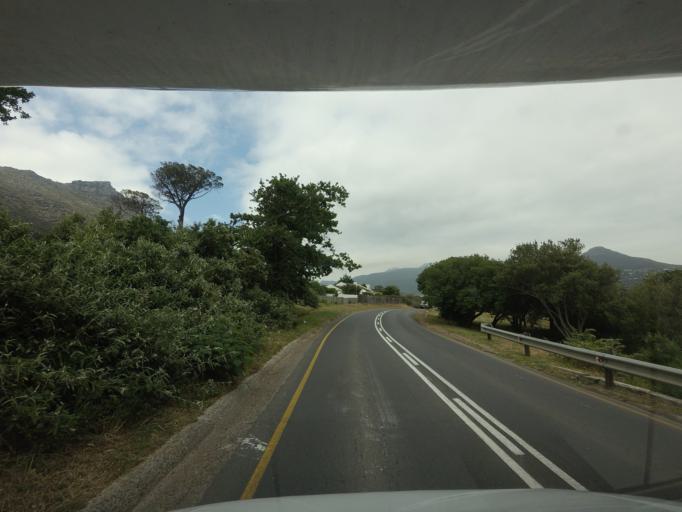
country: ZA
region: Western Cape
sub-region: City of Cape Town
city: Constantia
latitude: -34.0195
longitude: 18.3742
